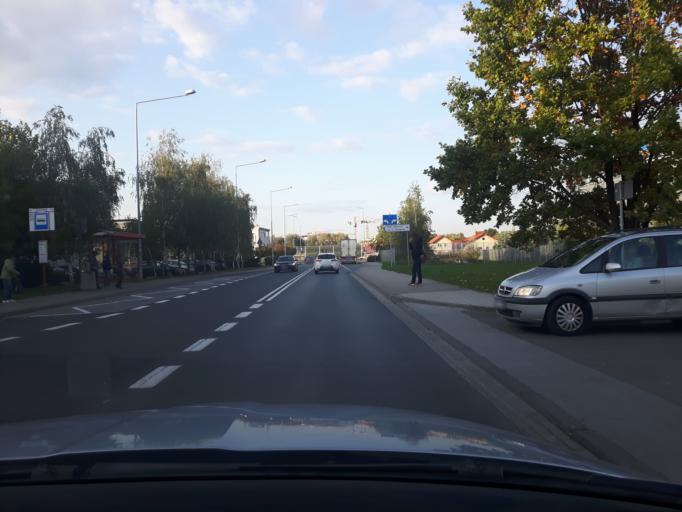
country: PL
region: Masovian Voivodeship
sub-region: Warszawa
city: Wlochy
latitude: 52.1551
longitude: 20.9946
